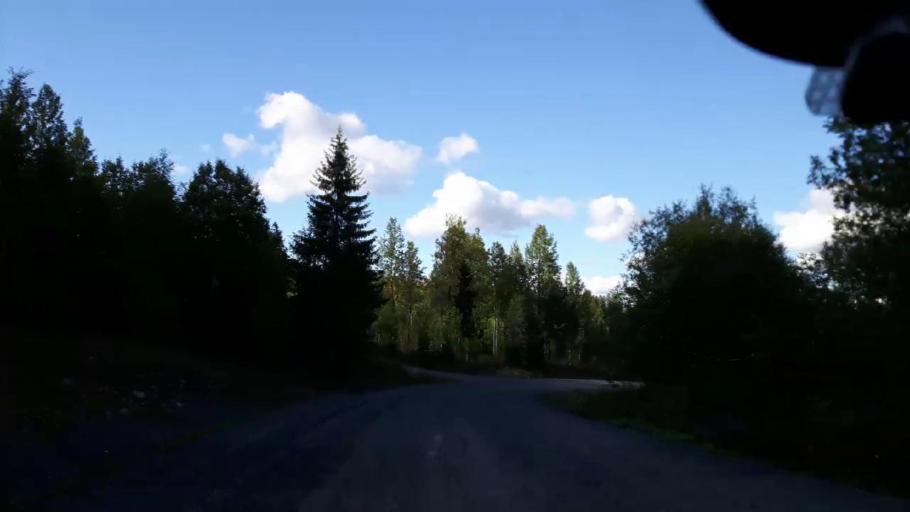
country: SE
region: Jaemtland
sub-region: Ragunda Kommun
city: Hammarstrand
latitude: 63.4356
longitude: 16.1875
